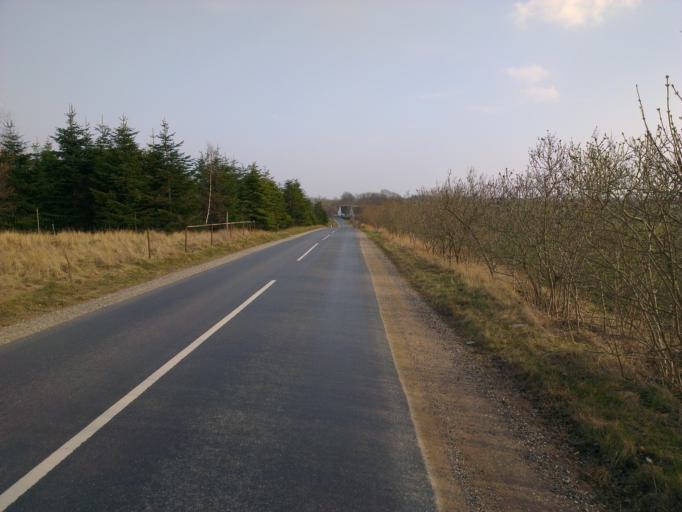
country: DK
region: Capital Region
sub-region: Frederikssund Kommune
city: Jaegerspris
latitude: 55.8275
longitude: 11.9647
